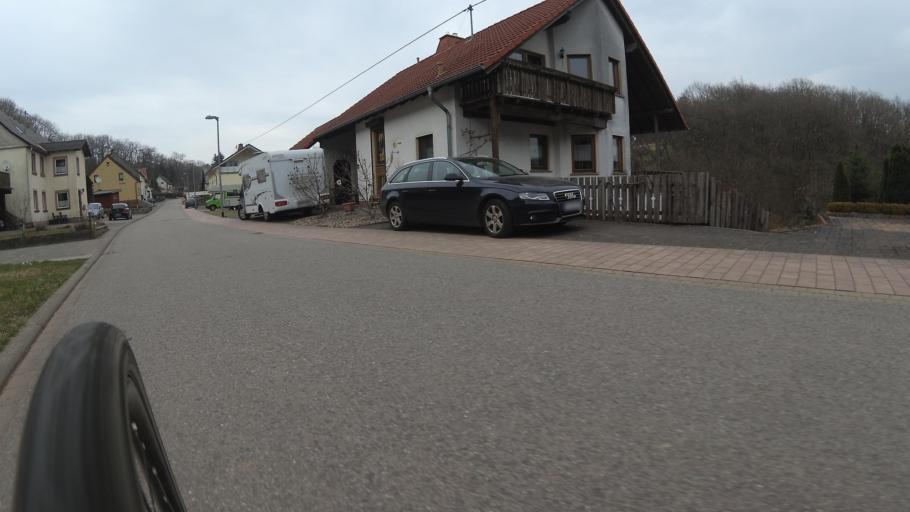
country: DE
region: Rheinland-Pfalz
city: Dienstweiler
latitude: 49.6380
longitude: 7.1866
